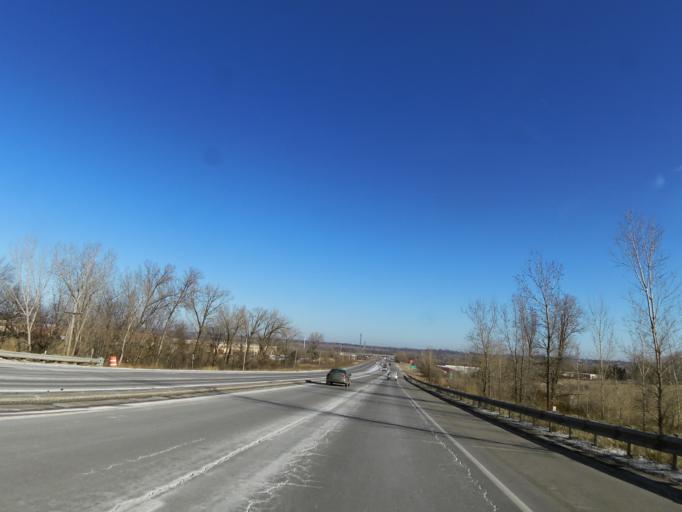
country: US
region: Minnesota
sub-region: Scott County
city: Savage
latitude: 44.7668
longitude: -93.3795
